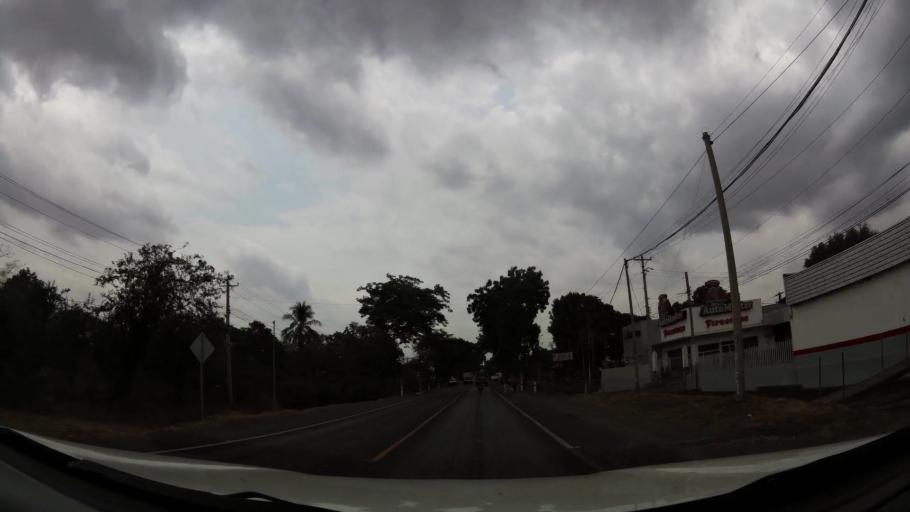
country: NI
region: Leon
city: Leon
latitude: 12.4616
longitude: -86.8672
